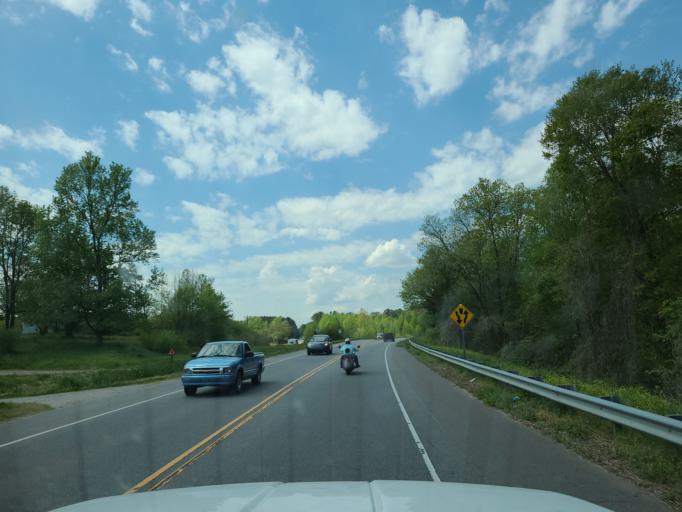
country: US
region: North Carolina
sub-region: Lincoln County
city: Lincolnton
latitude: 35.4281
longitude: -81.2939
